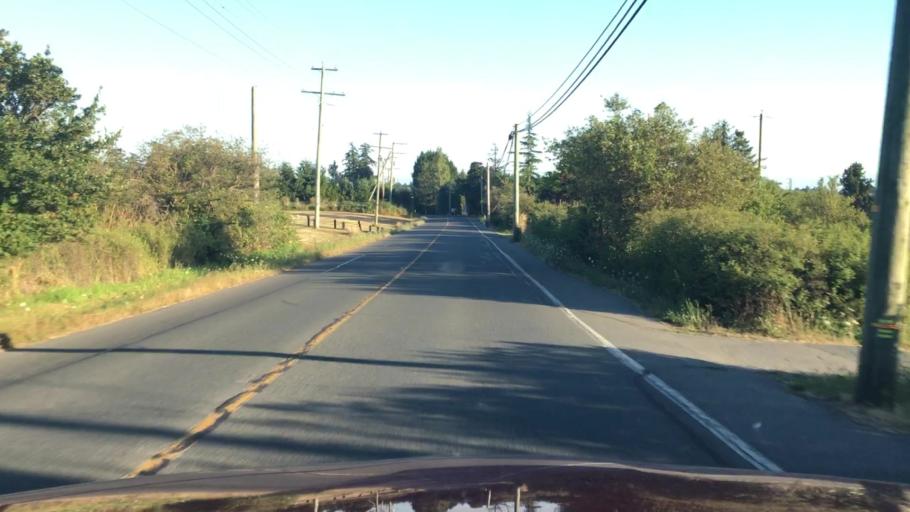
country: CA
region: British Columbia
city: Victoria
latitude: 48.4819
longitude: -123.3547
